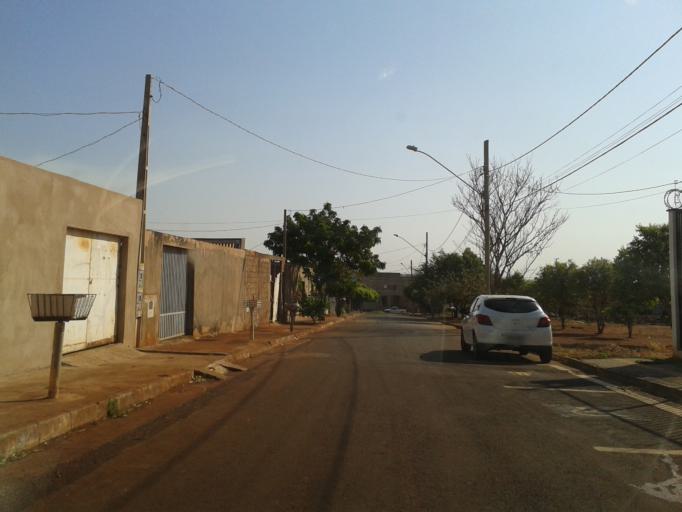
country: BR
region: Minas Gerais
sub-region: Ituiutaba
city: Ituiutaba
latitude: -18.9786
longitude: -49.4370
